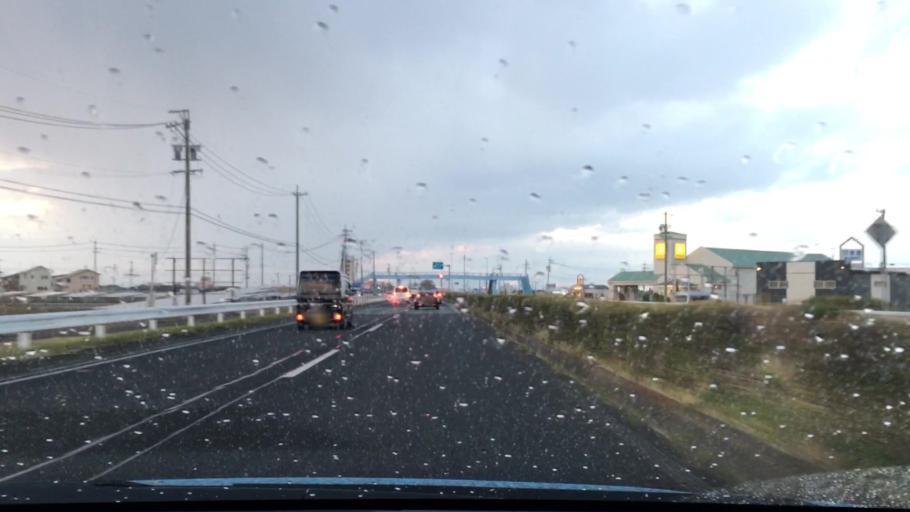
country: JP
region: Mie
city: Ise
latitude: 34.5674
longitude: 136.6353
